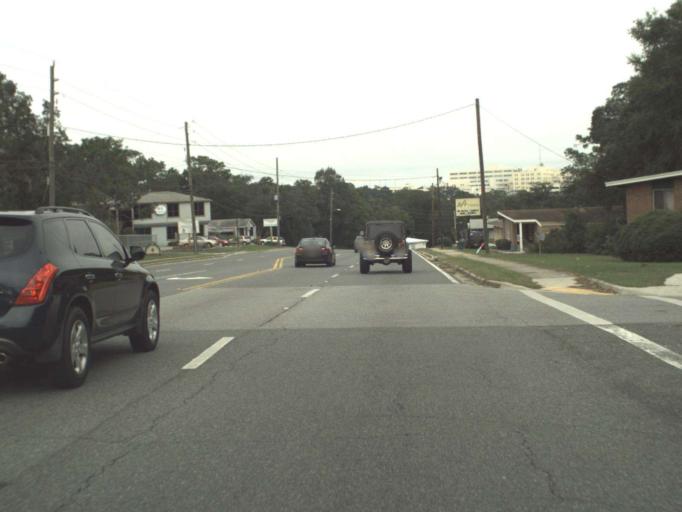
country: US
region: Florida
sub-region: Escambia County
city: Brent
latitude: 30.4749
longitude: -87.2213
